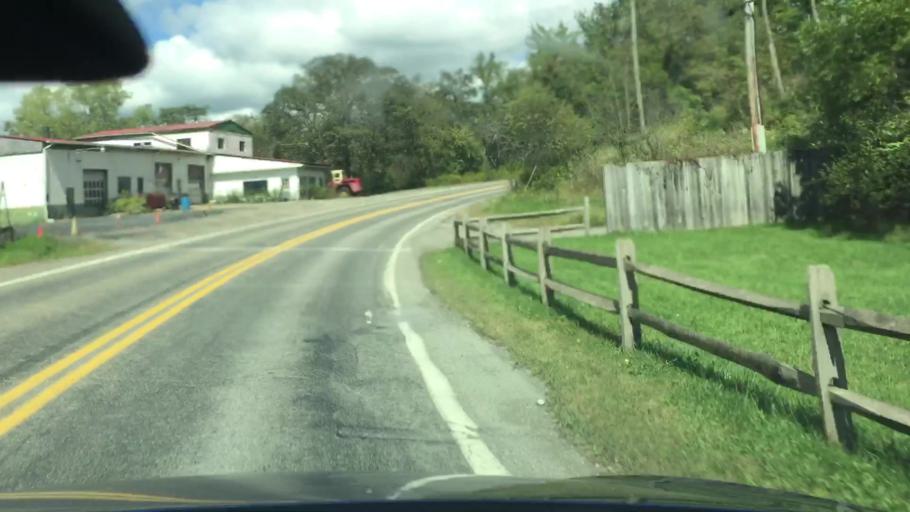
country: US
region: Pennsylvania
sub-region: Allegheny County
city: Russellton
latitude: 40.6219
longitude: -79.8337
